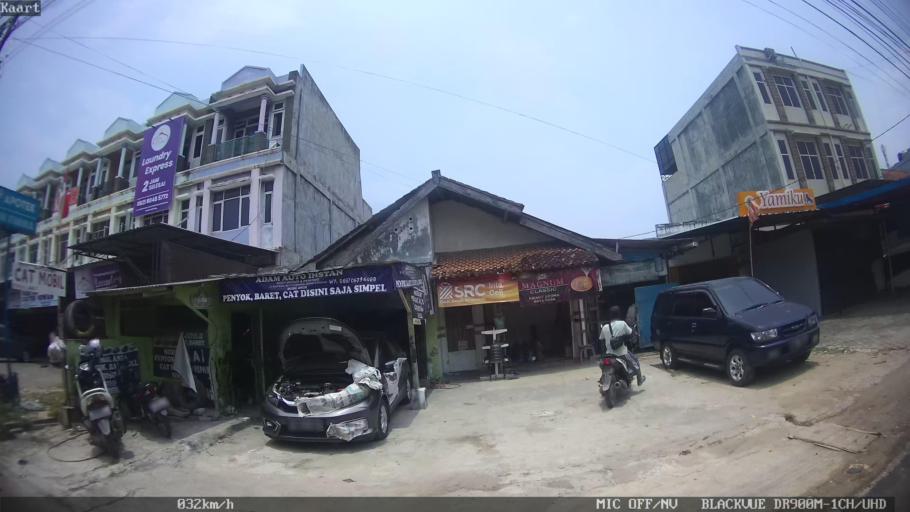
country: ID
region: Lampung
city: Bandarlampung
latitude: -5.4114
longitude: 105.2837
